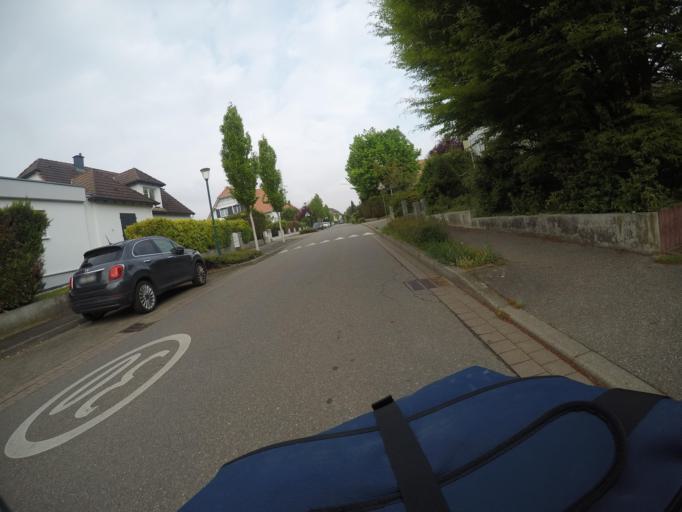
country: FR
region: Alsace
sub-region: Departement du Bas-Rhin
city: Wolfisheim
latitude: 48.5852
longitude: 7.6631
